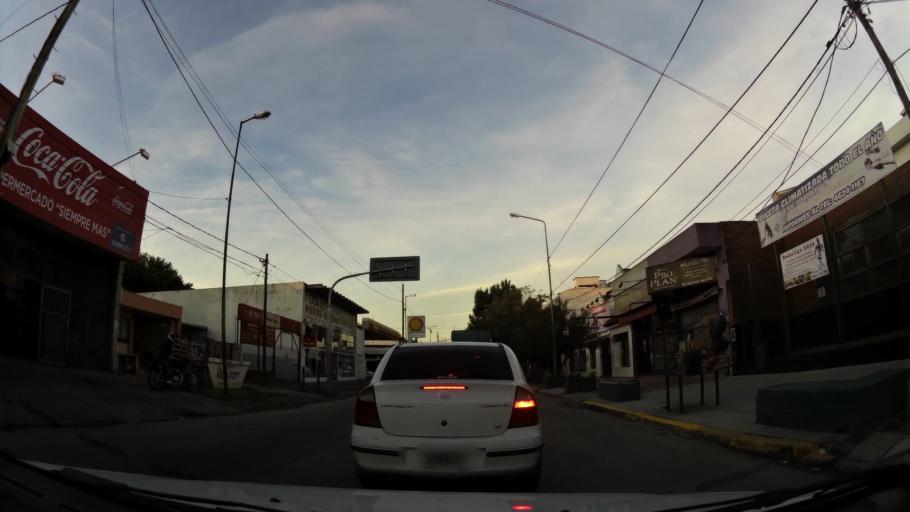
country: AR
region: Buenos Aires
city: Ituzaingo
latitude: -34.6491
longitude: -58.6582
